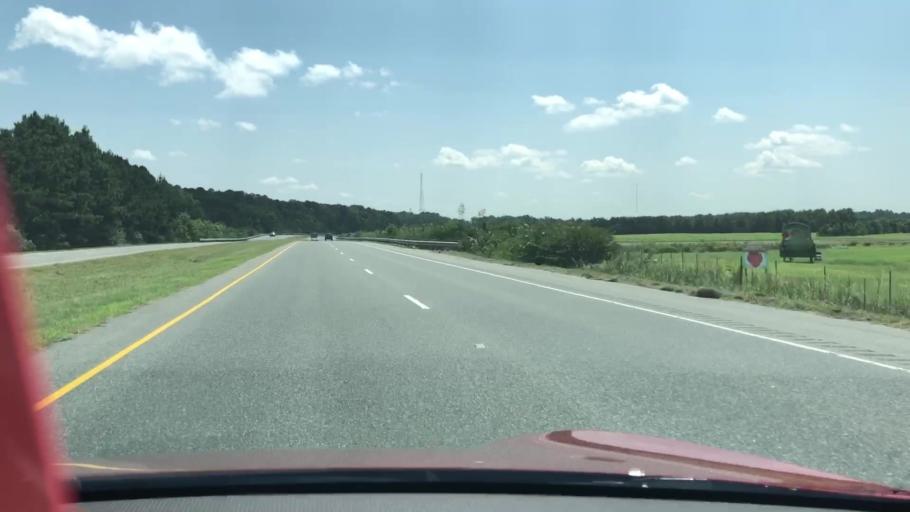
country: US
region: North Carolina
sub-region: Currituck County
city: Moyock
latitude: 36.6481
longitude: -76.2234
